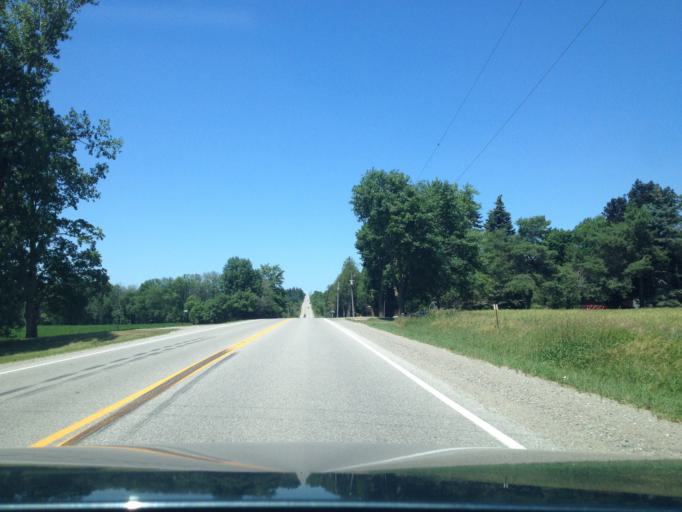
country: CA
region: Ontario
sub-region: Wellington County
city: Guelph
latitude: 43.6763
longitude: -80.2997
